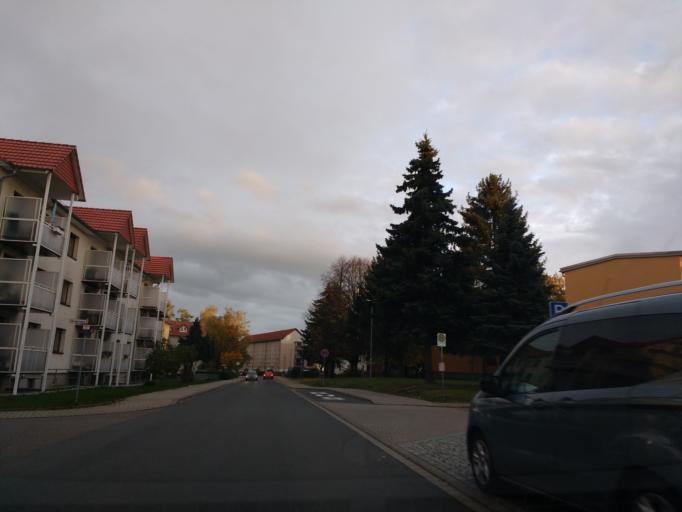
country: DE
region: Thuringia
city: Leinefelde
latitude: 51.3867
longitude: 10.3242
